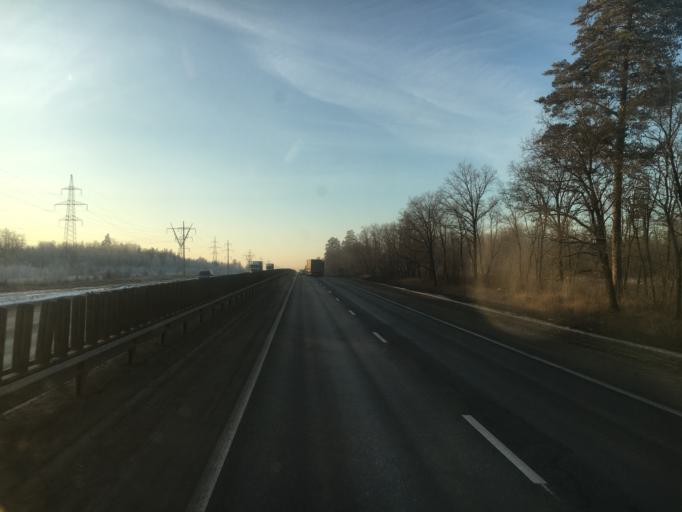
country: RU
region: Samara
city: Pribrezhnyy
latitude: 53.5155
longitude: 49.8719
